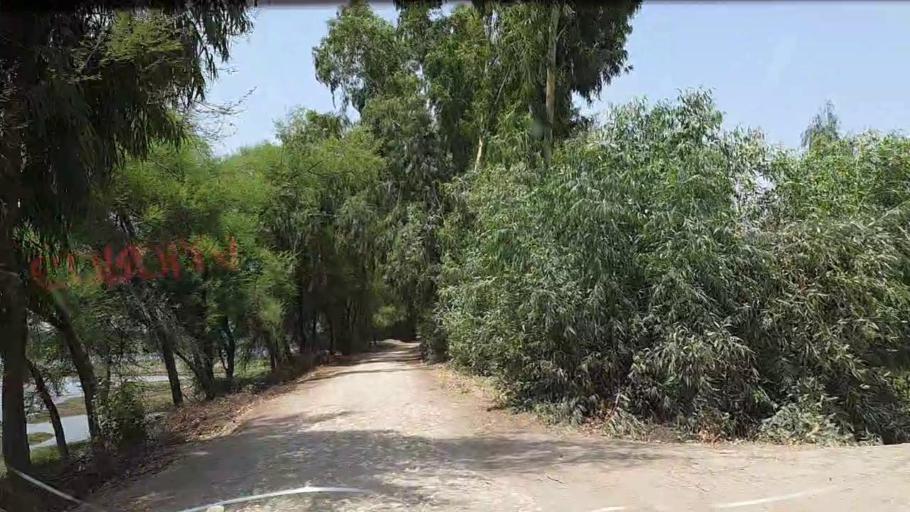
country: PK
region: Sindh
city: Ghotki
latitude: 28.0868
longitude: 69.3110
